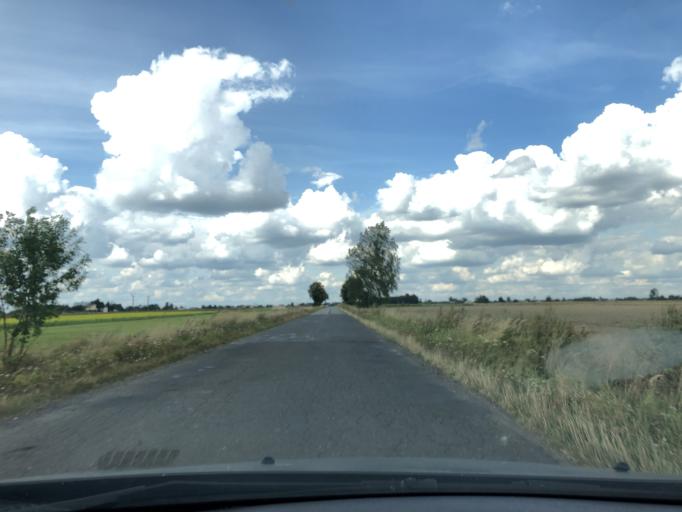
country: PL
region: Lodz Voivodeship
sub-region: Powiat wieruszowski
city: Walichnowy
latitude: 51.2499
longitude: 18.3897
